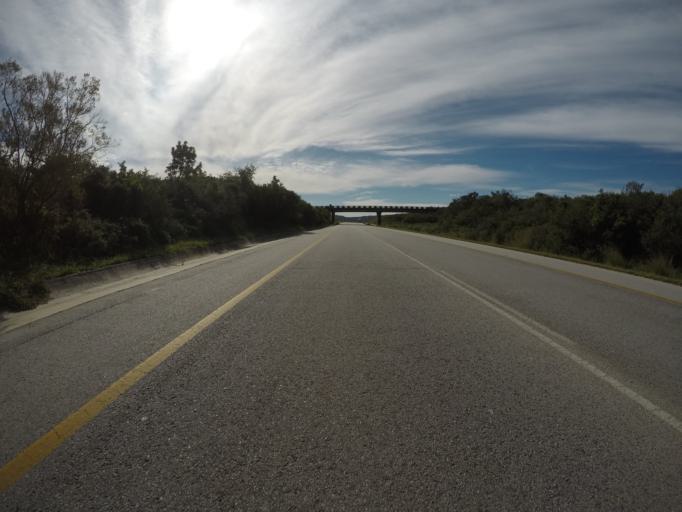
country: ZA
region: Eastern Cape
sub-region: Cacadu District Municipality
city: Jeffrey's Bay
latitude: -33.8977
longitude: 25.1202
